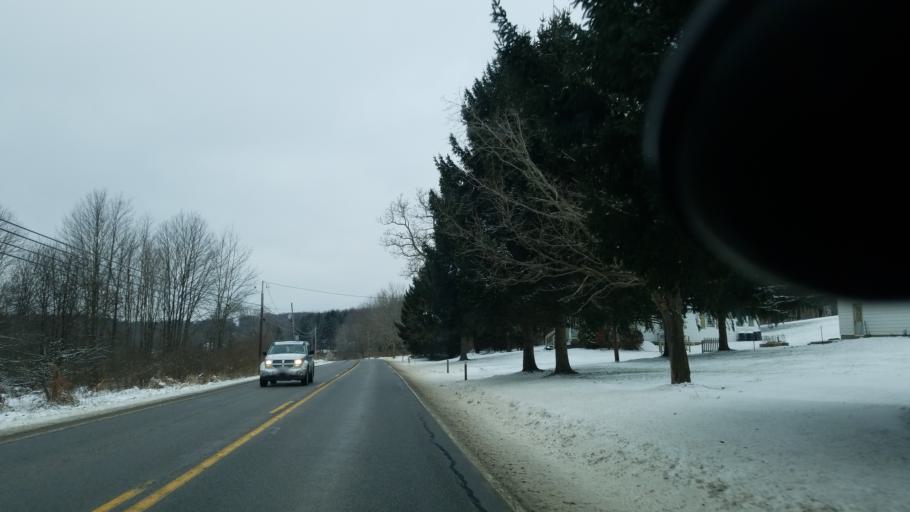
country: US
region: Pennsylvania
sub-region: Indiana County
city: Johnsonburg
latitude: 40.9305
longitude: -78.9009
